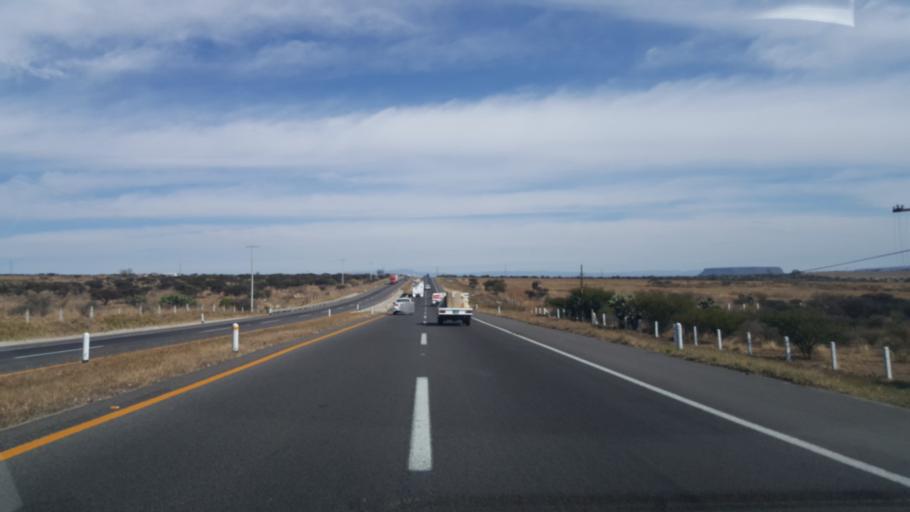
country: MX
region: Jalisco
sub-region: Lagos de Moreno
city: Cristeros [Fraccionamiento]
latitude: 21.3038
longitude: -102.0989
